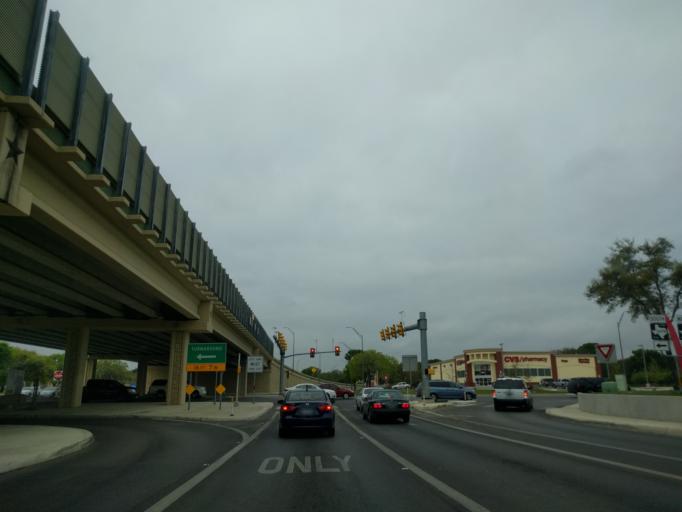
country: US
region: Texas
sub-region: Bexar County
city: Castle Hills
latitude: 29.5588
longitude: -98.5166
